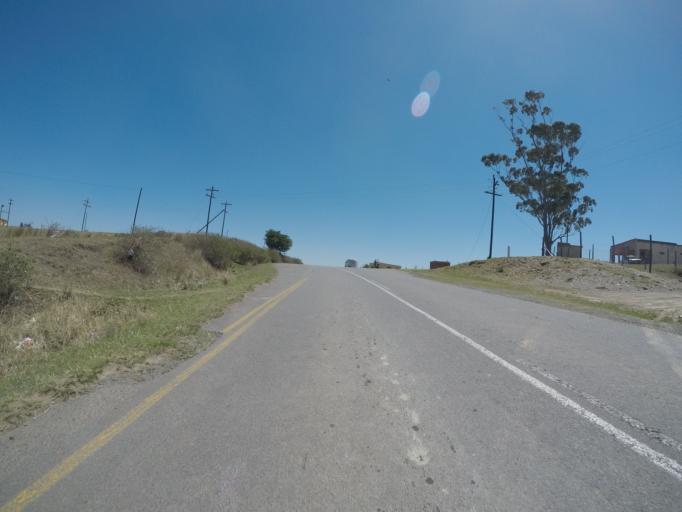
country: ZA
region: Eastern Cape
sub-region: OR Tambo District Municipality
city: Libode
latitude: -31.9085
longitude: 29.0045
